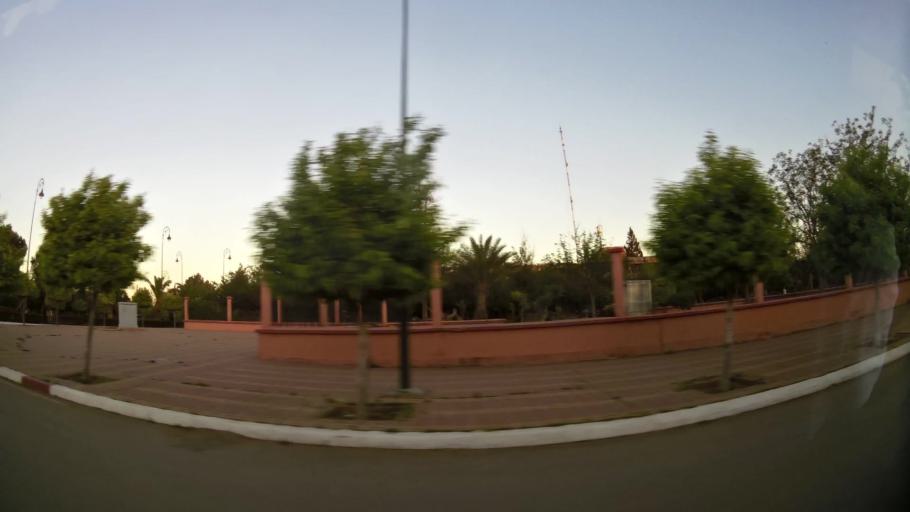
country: MA
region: Marrakech-Tensift-Al Haouz
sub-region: Kelaa-Des-Sraghna
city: Sidi Bou Othmane
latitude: 32.2140
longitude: -7.9287
